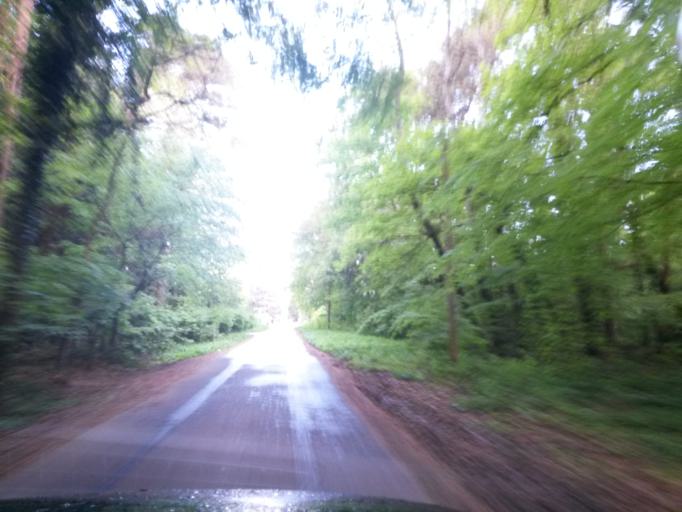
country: DE
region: North Rhine-Westphalia
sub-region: Regierungsbezirk Koln
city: Alfter
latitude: 50.6905
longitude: 7.0381
